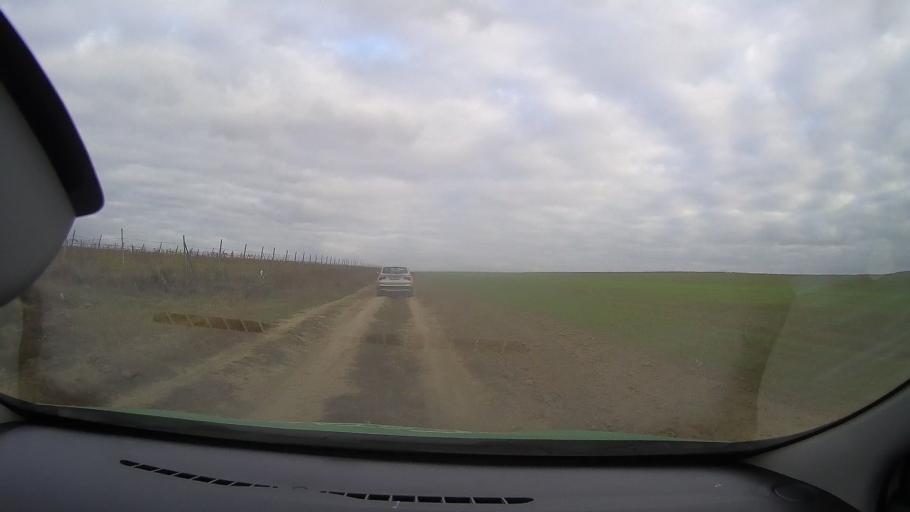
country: RO
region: Tulcea
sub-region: Comuna Jurilovca
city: Jurilovca
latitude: 44.7652
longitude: 28.9070
